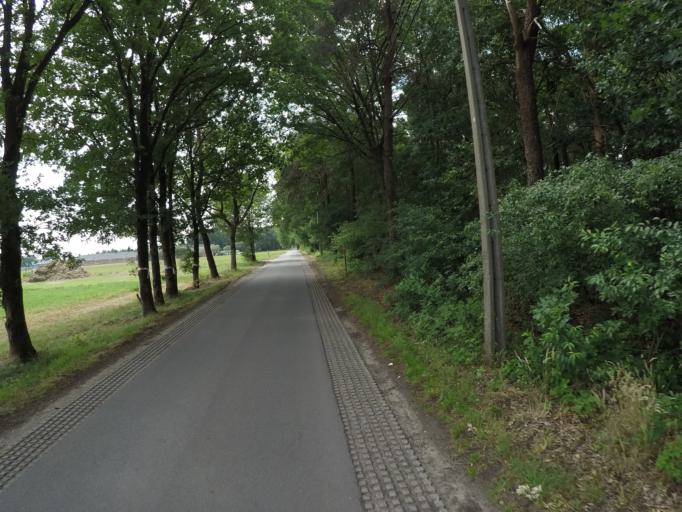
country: BE
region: Flanders
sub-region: Provincie Antwerpen
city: Essen
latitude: 51.4584
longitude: 4.5297
